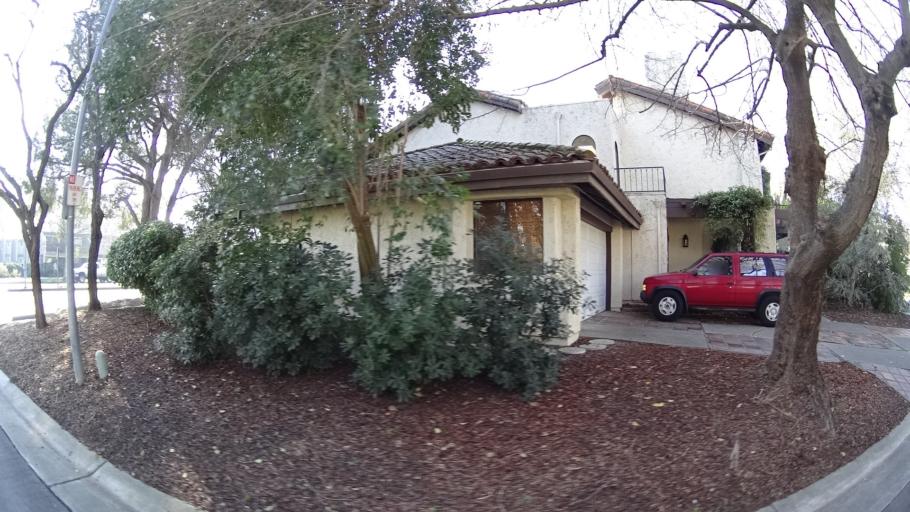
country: US
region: California
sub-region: Yolo County
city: Davis
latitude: 38.5504
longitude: -121.7880
